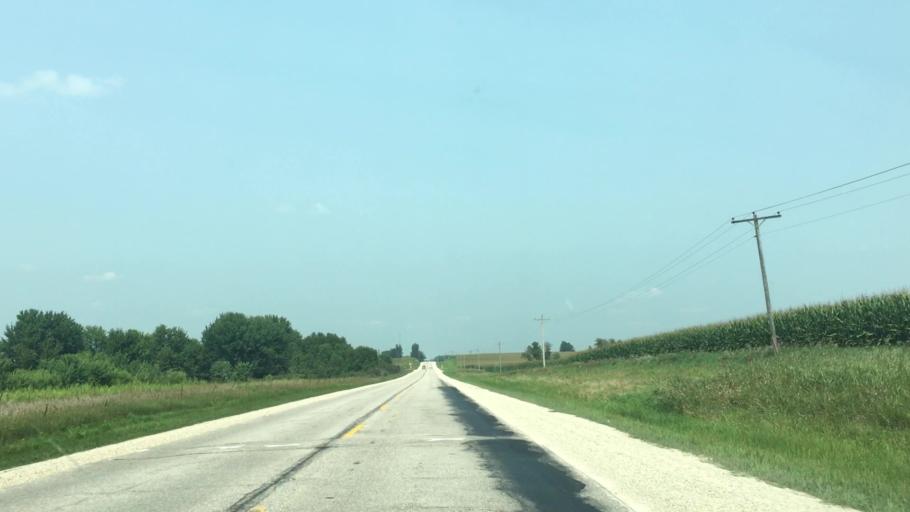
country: US
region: Iowa
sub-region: Buchanan County
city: Independence
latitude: 42.3595
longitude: -91.8893
